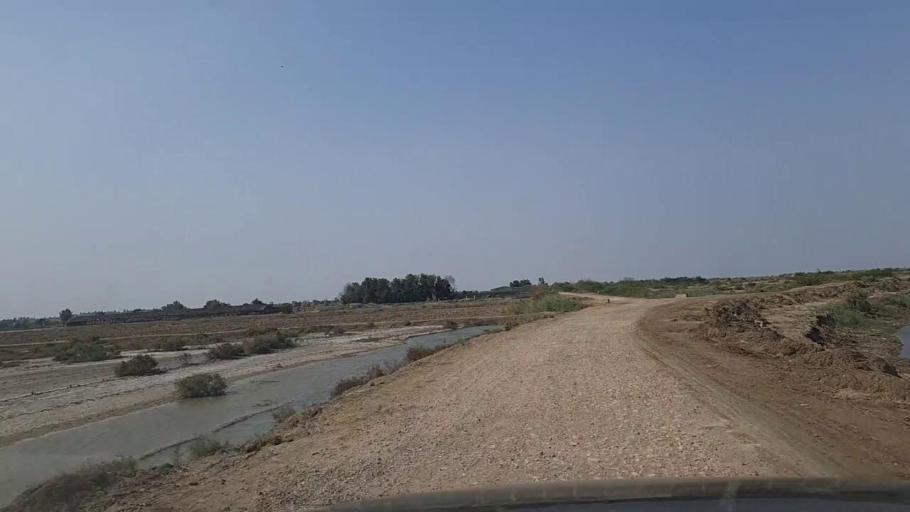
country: PK
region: Sindh
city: Gharo
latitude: 24.7019
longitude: 67.5860
